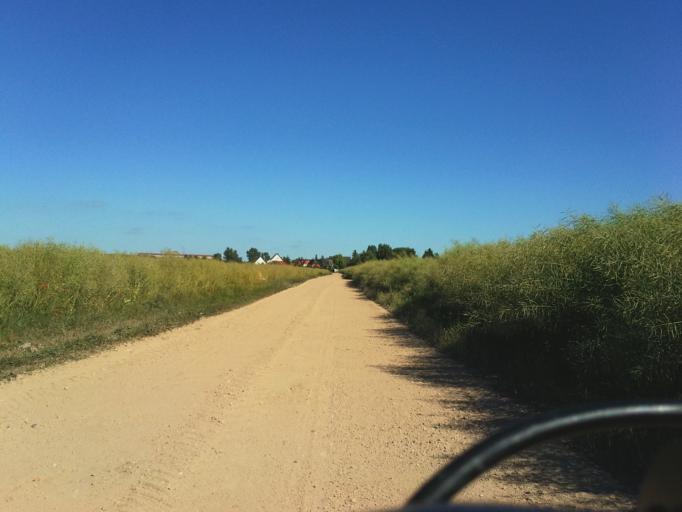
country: DE
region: Mecklenburg-Vorpommern
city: Monchhagen
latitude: 54.1630
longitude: 12.2195
